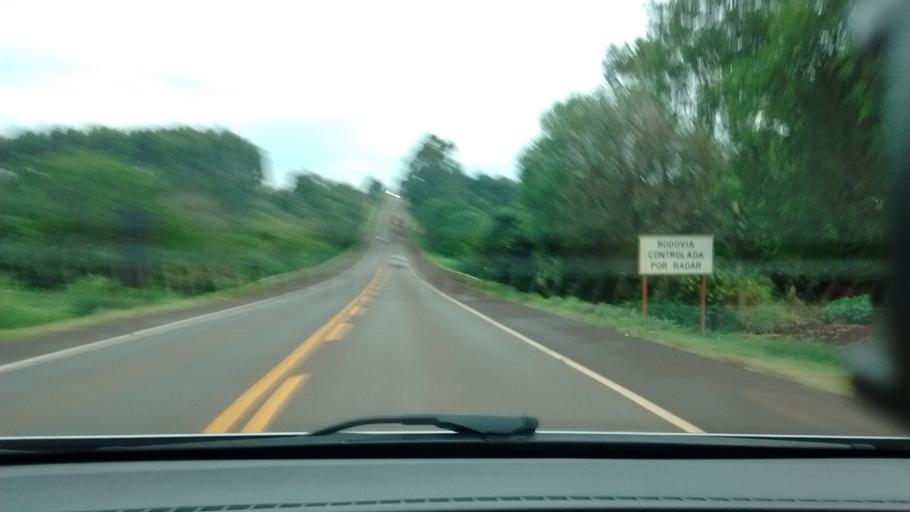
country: BR
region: Parana
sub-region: Corbelia
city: Corbelia
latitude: -24.8081
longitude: -53.2932
